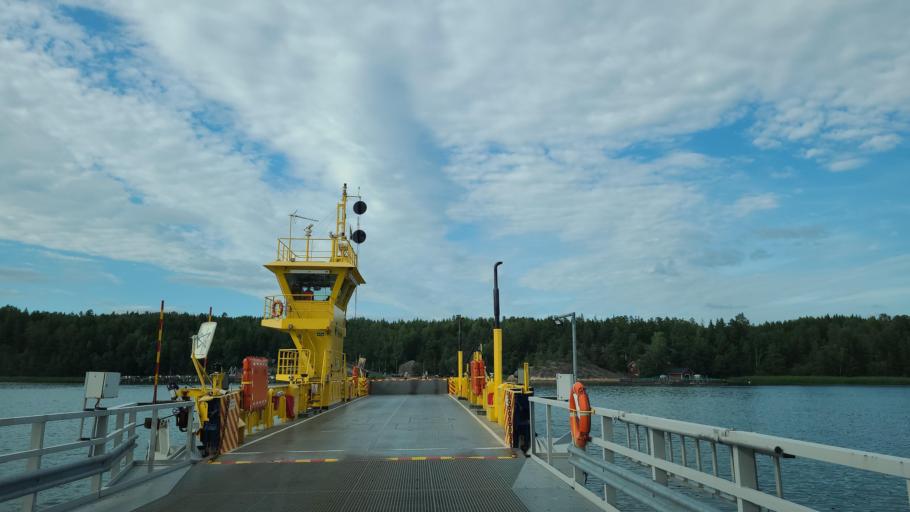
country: FI
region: Varsinais-Suomi
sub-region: Turku
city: Rymaettylae
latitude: 60.3137
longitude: 21.9615
